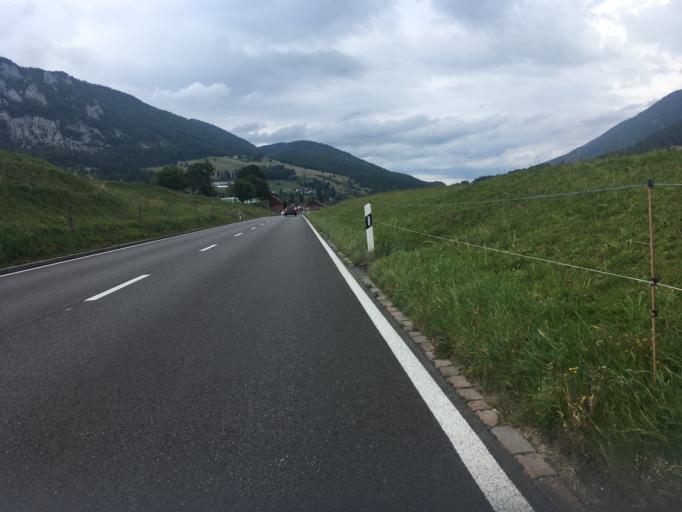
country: CH
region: Solothurn
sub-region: Bezirk Thal
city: Welschenrohr
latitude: 47.2747
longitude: 7.5155
